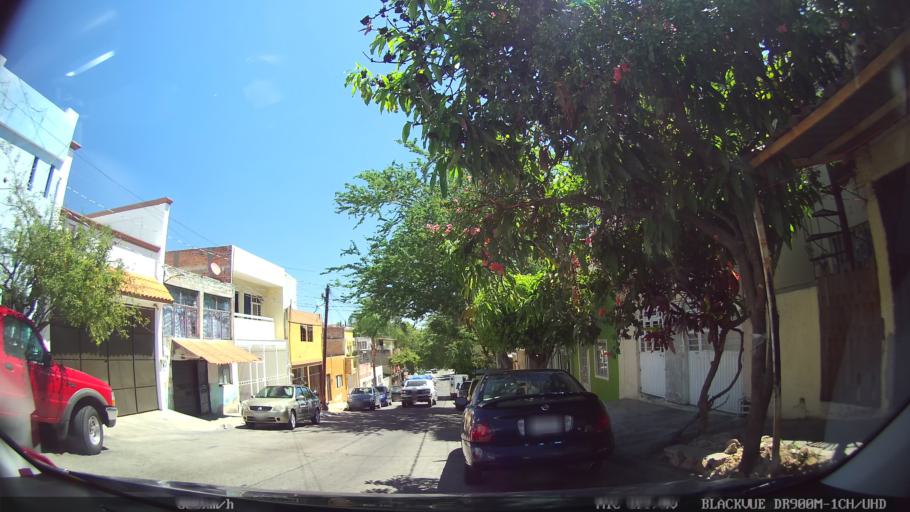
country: MX
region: Jalisco
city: Tlaquepaque
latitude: 20.6927
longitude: -103.2900
